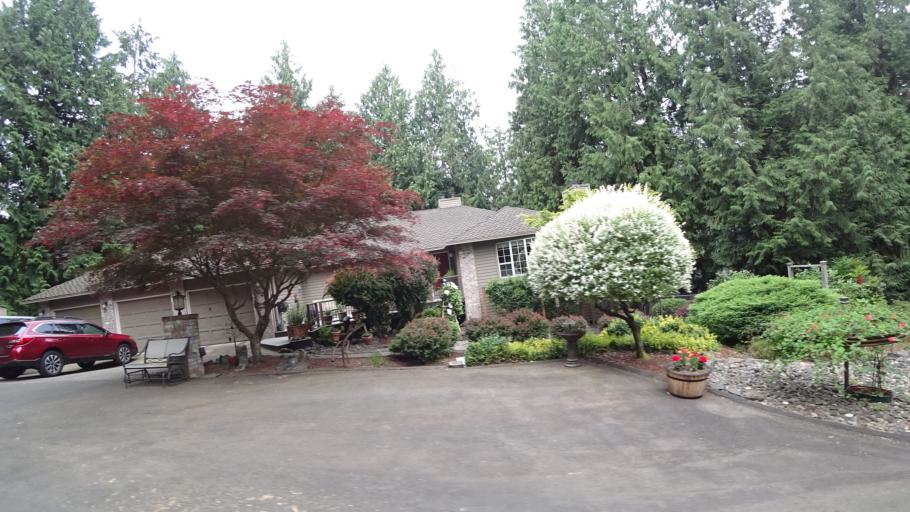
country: US
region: Oregon
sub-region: Washington County
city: Garden Home-Whitford
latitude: 45.4699
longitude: -122.7450
